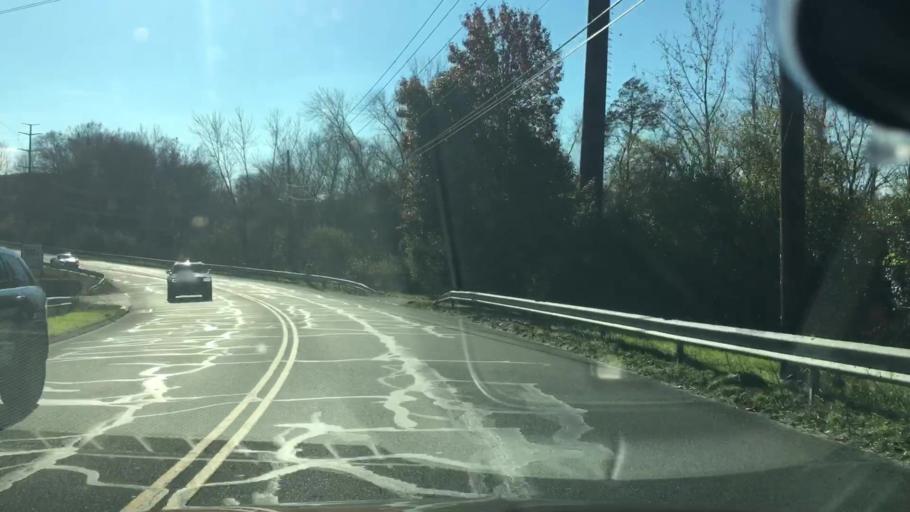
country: US
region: Connecticut
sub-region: Fairfield County
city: Bethel
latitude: 41.4435
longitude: -73.3958
